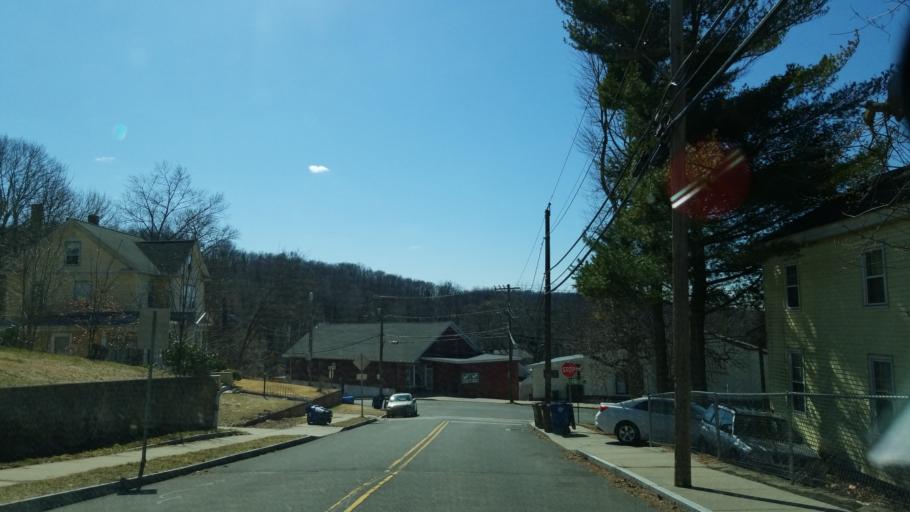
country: US
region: Connecticut
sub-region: Tolland County
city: Rockville
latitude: 41.8690
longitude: -72.4432
